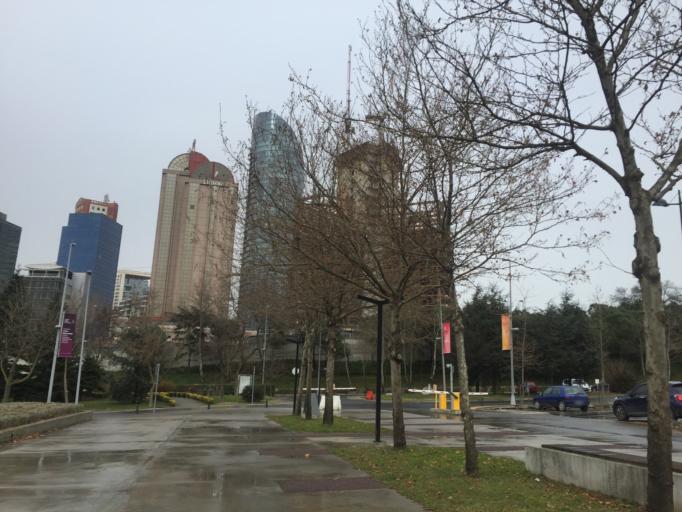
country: TR
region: Istanbul
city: Sisli
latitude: 41.1072
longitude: 29.0236
